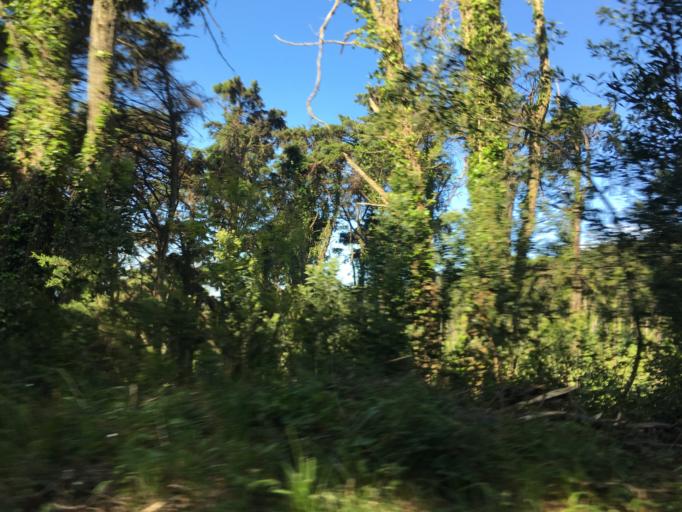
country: PT
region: Lisbon
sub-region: Sintra
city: Colares
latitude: 38.7711
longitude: -9.4469
